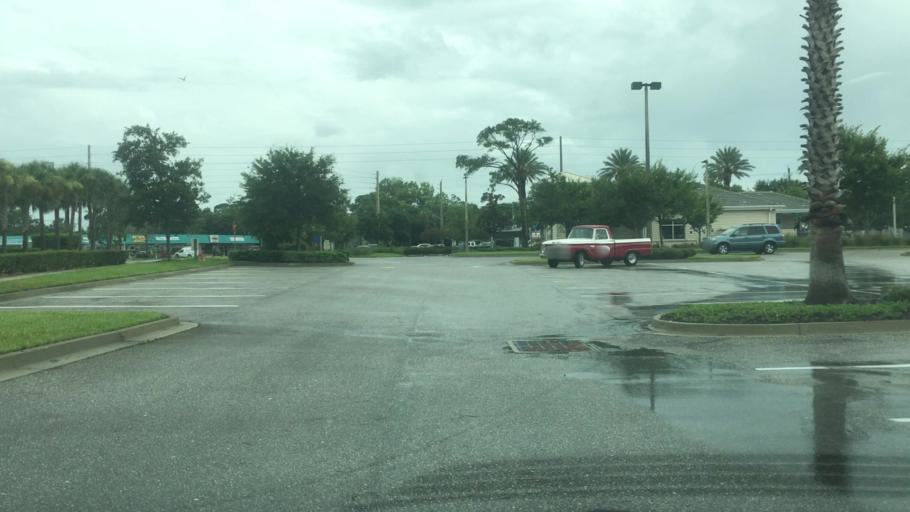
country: US
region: Florida
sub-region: Duval County
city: Atlantic Beach
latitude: 30.3233
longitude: -81.4056
